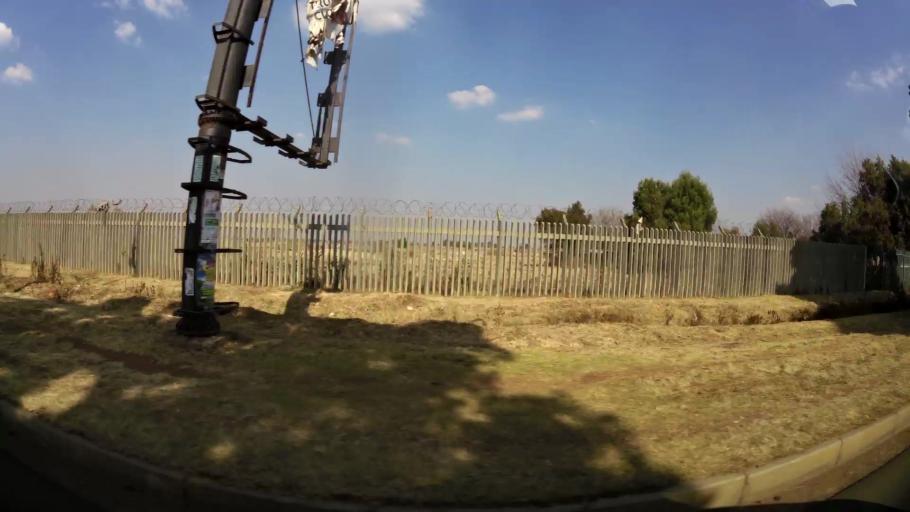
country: ZA
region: Gauteng
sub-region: Ekurhuleni Metropolitan Municipality
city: Brakpan
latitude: -26.1593
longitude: 28.4111
